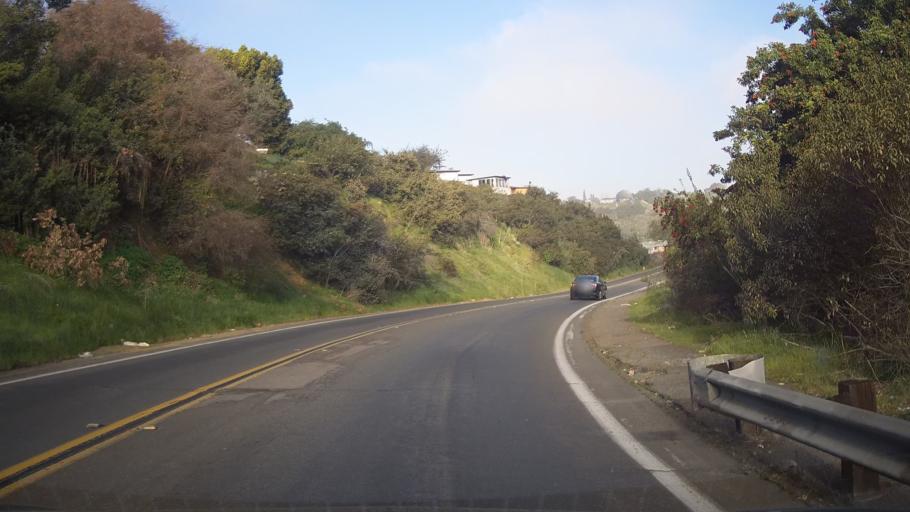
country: US
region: California
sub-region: San Diego County
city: National City
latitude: 32.7276
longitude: -117.0871
